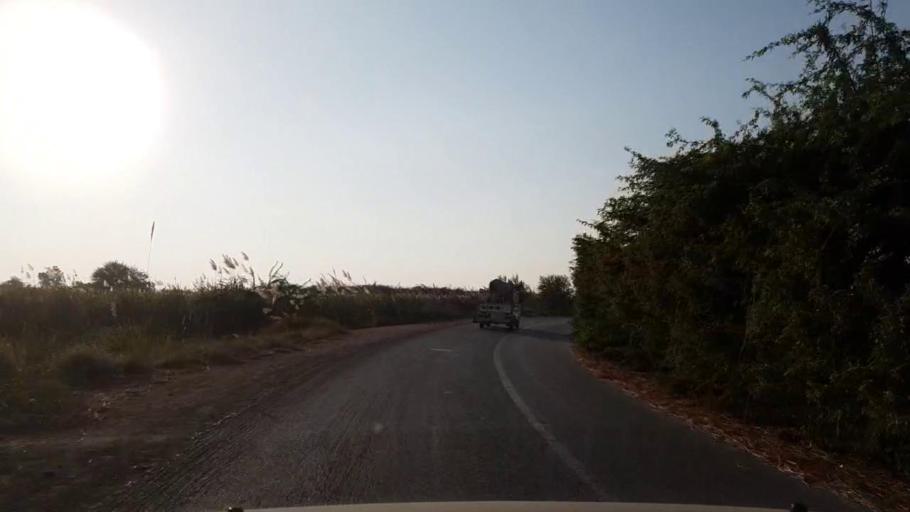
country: PK
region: Sindh
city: Mirpur Batoro
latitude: 24.6896
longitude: 68.1804
